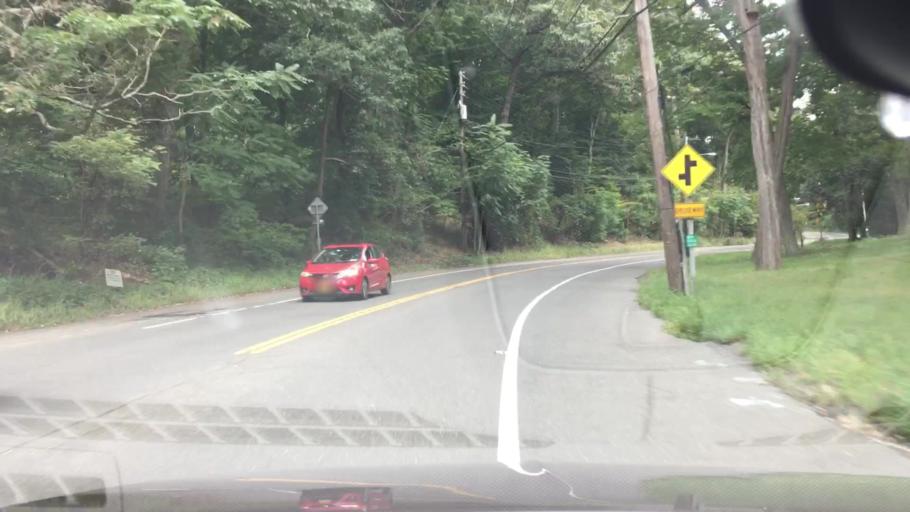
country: US
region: New York
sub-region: Suffolk County
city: Head of the Harbor
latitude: 40.9049
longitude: -73.1405
